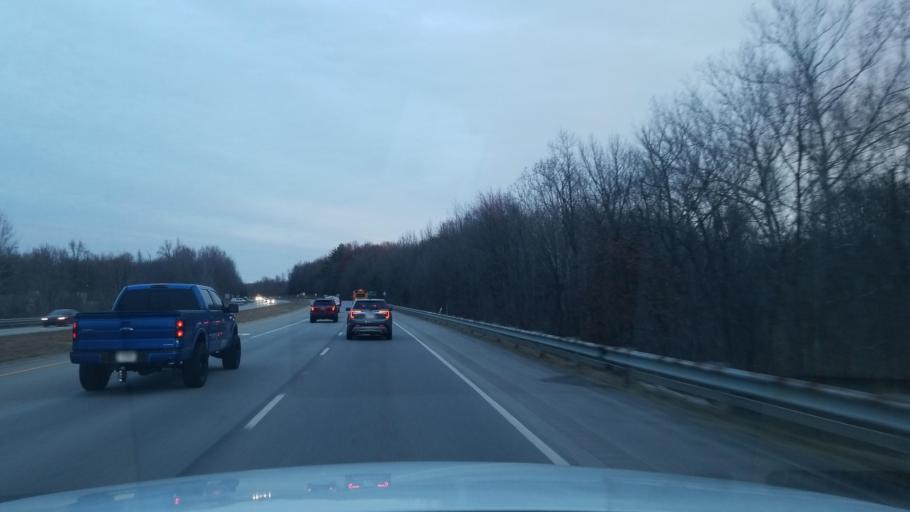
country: US
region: Indiana
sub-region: Vanderburgh County
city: Evansville
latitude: 37.9497
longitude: -87.7017
